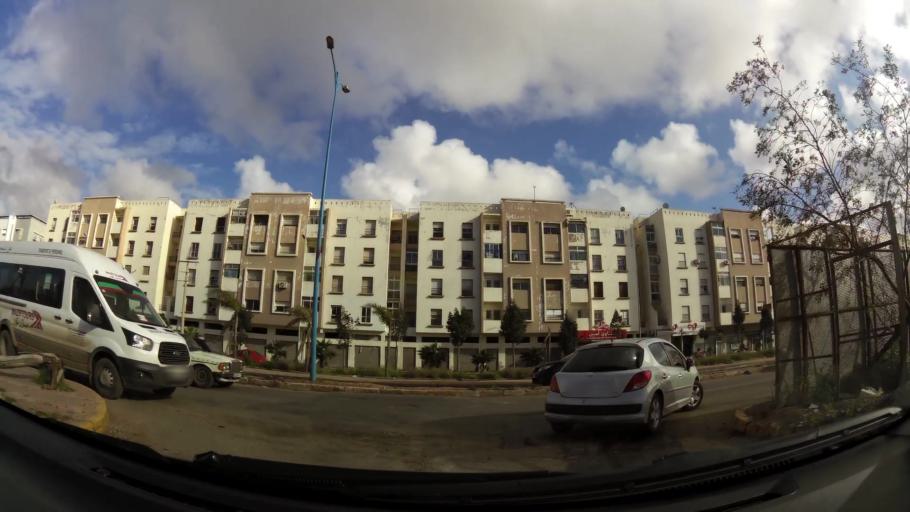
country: MA
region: Grand Casablanca
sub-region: Casablanca
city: Casablanca
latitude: 33.5491
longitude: -7.7003
